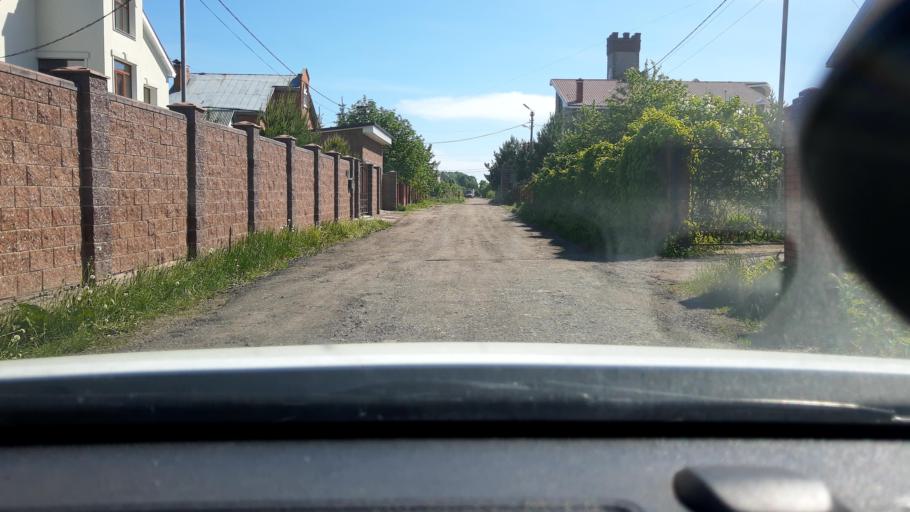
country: RU
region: Bashkortostan
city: Avdon
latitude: 54.5041
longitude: 55.8205
